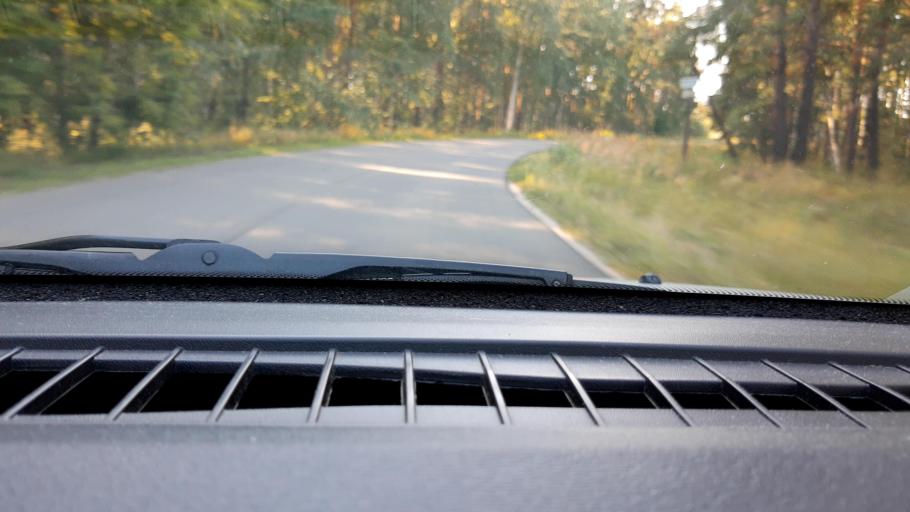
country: RU
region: Nizjnij Novgorod
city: Babino
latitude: 56.3316
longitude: 43.6203
